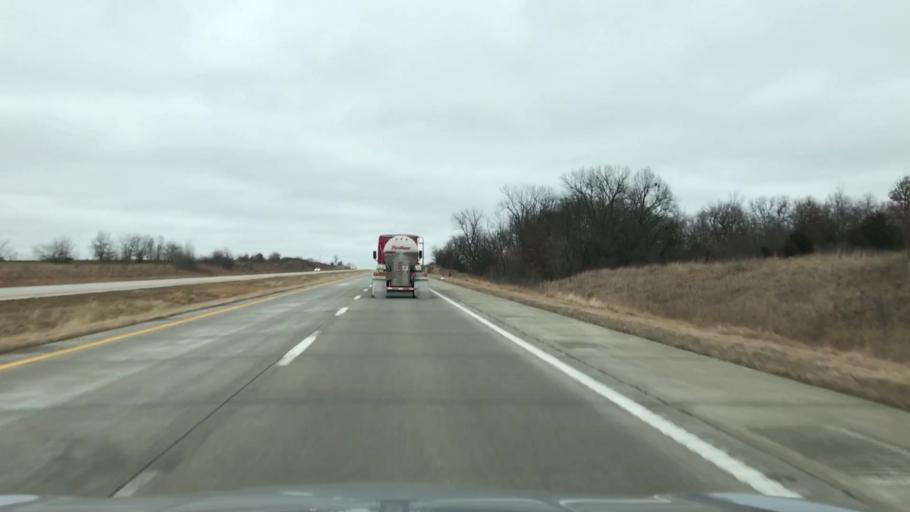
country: US
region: Missouri
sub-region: Caldwell County
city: Hamilton
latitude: 39.7351
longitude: -93.9384
